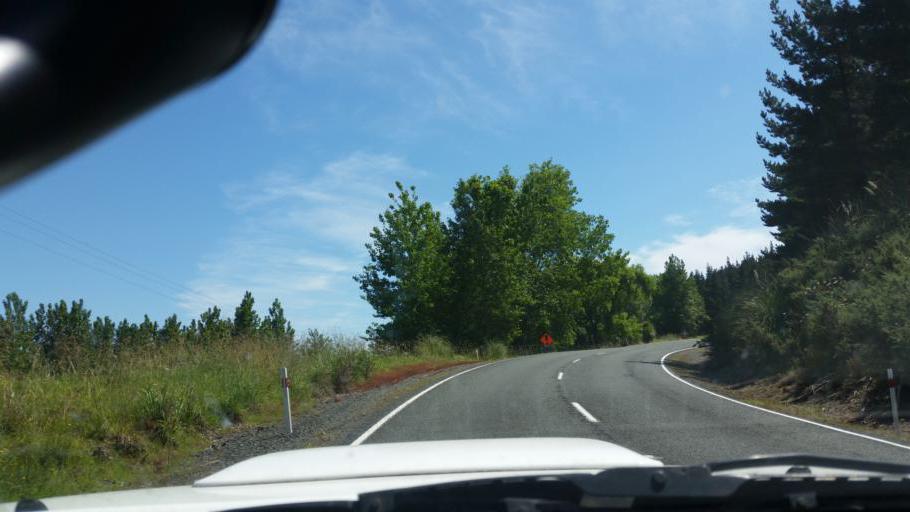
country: NZ
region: Auckland
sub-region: Auckland
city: Wellsford
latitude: -36.2083
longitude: 174.3920
